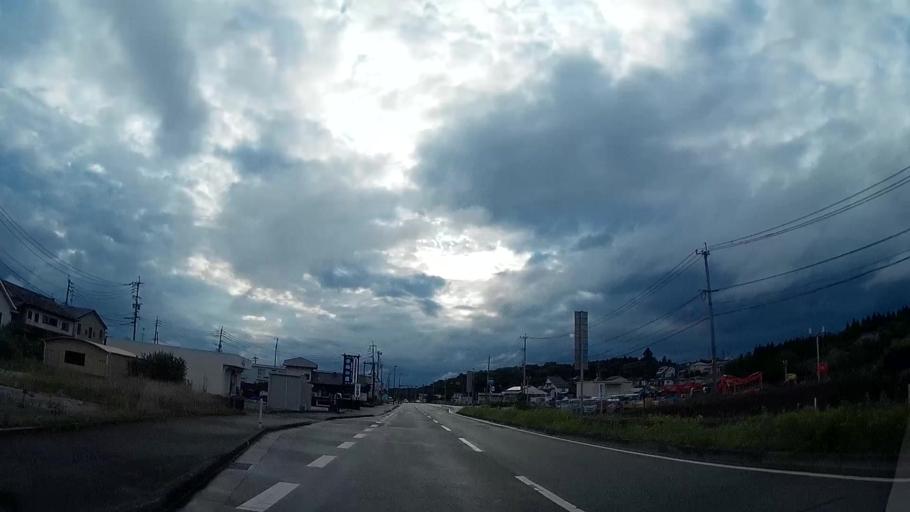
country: JP
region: Kumamoto
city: Ozu
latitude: 32.8799
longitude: 130.9027
